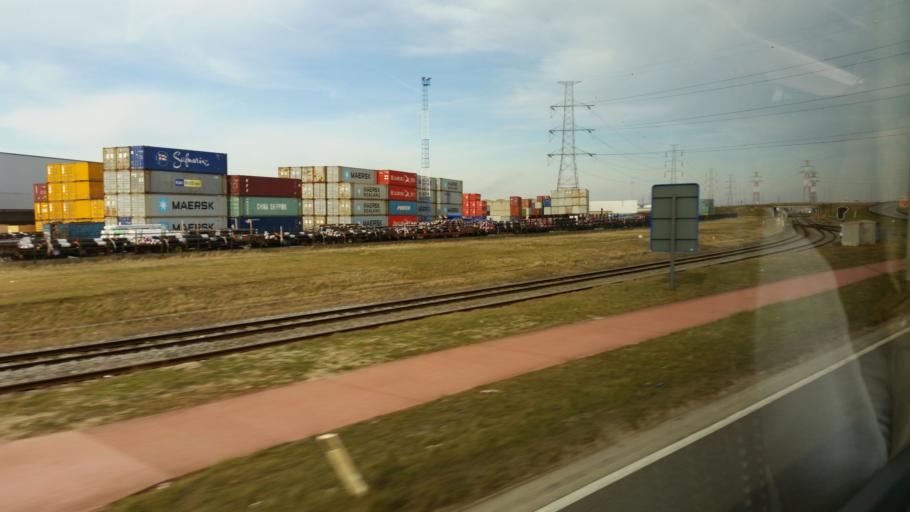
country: BE
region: Flanders
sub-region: Provincie Oost-Vlaanderen
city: Beveren
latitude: 51.2500
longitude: 4.2510
